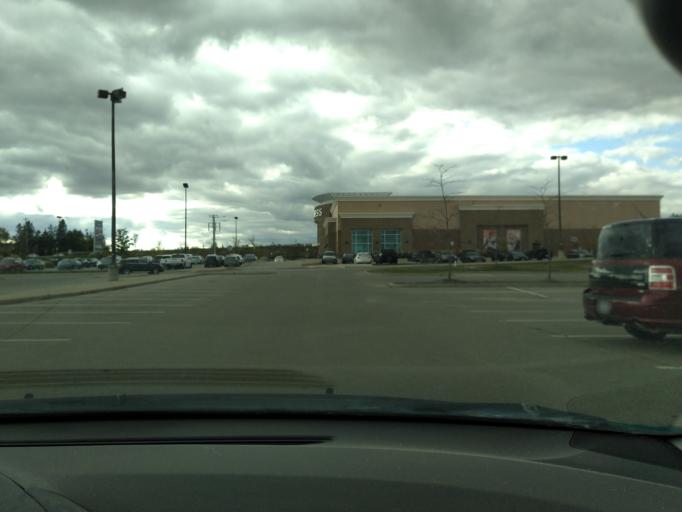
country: CA
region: Ontario
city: Newmarket
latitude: 44.0766
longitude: -79.4831
